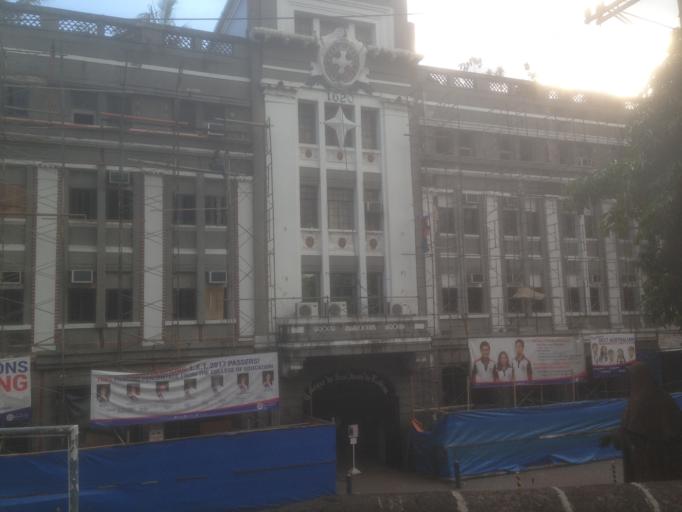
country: PH
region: Metro Manila
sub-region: City of Manila
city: Quiapo
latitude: 14.5937
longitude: 120.9775
